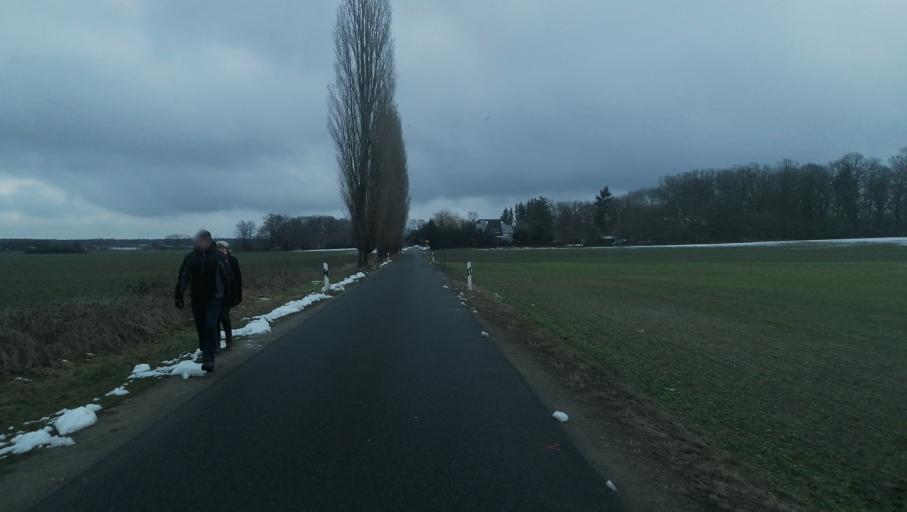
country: DE
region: Brandenburg
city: Cottbus
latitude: 51.6805
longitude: 14.3482
